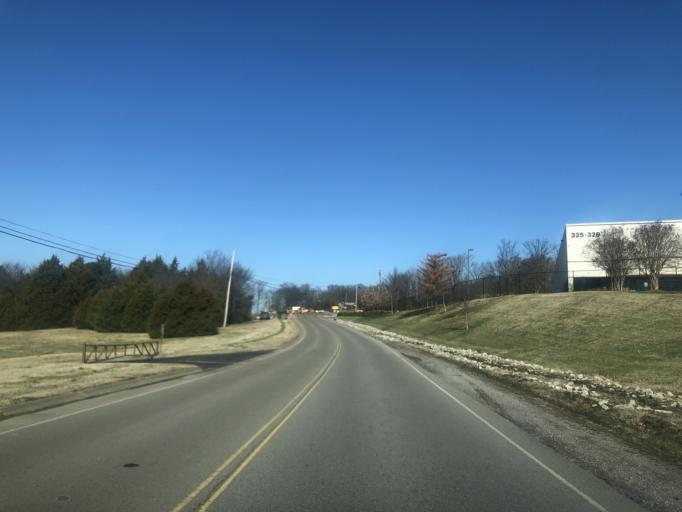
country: US
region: Tennessee
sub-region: Rutherford County
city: La Vergne
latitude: 35.9991
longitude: -86.5856
